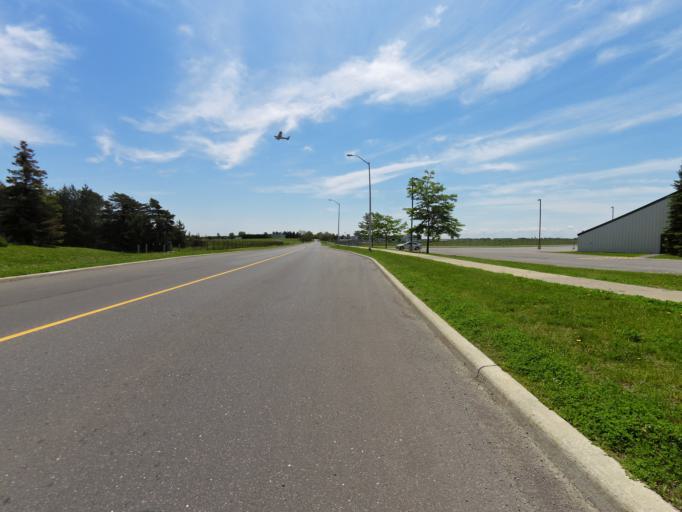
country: CA
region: Ontario
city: Ottawa
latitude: 45.3370
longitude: -75.6842
